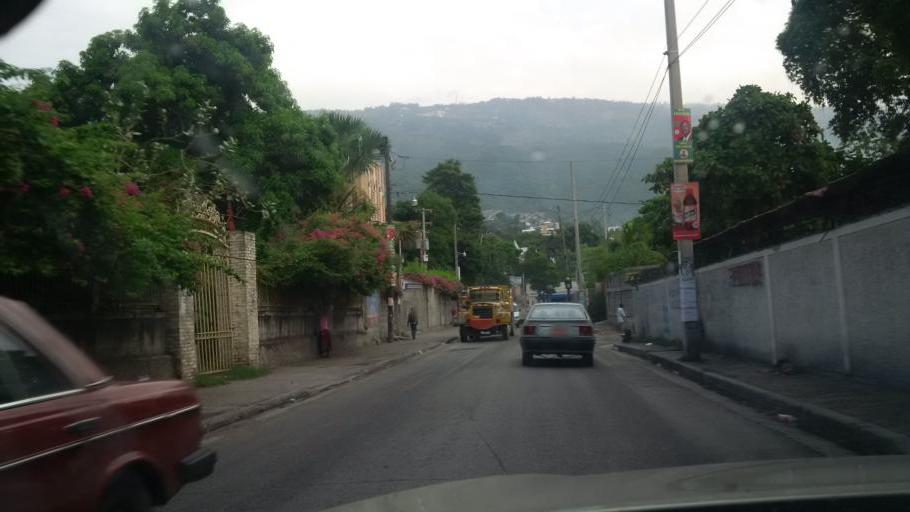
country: HT
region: Ouest
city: Port-au-Prince
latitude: 18.5350
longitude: -72.3336
